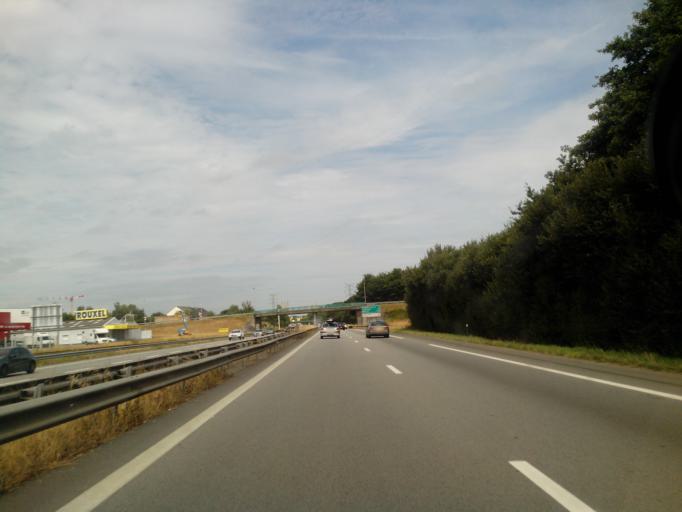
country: FR
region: Brittany
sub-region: Departement du Morbihan
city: Vannes
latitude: 47.6675
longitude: -2.7315
